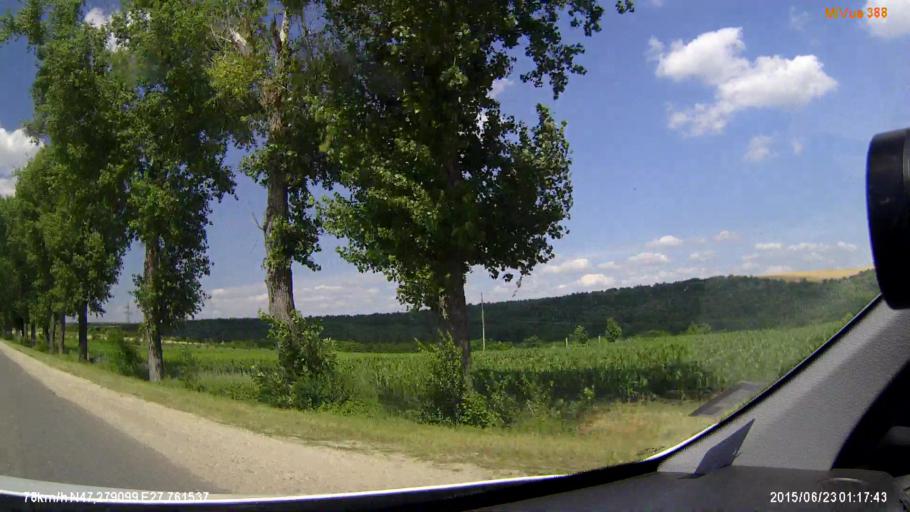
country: RO
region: Iasi
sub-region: Comuna Ungheni
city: Bosia
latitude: 47.2789
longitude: 27.7615
